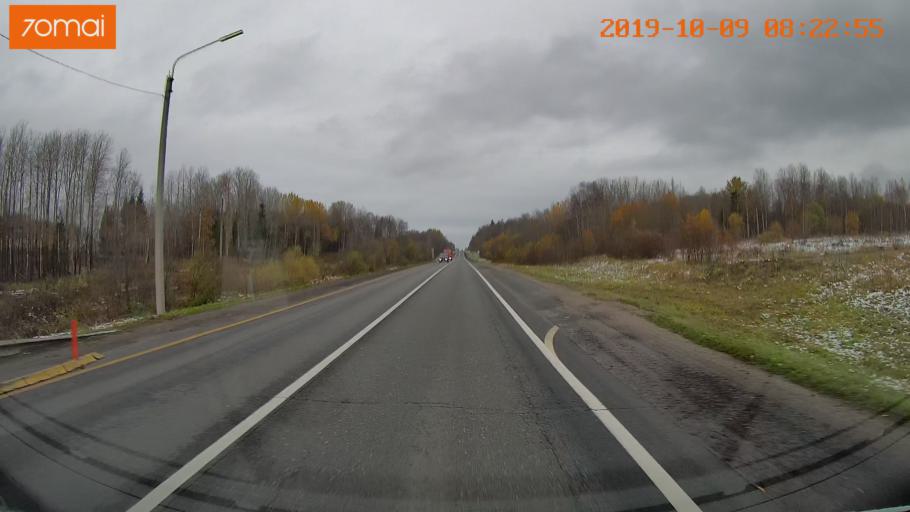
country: RU
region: Vologda
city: Gryazovets
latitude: 58.7477
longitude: 40.2862
